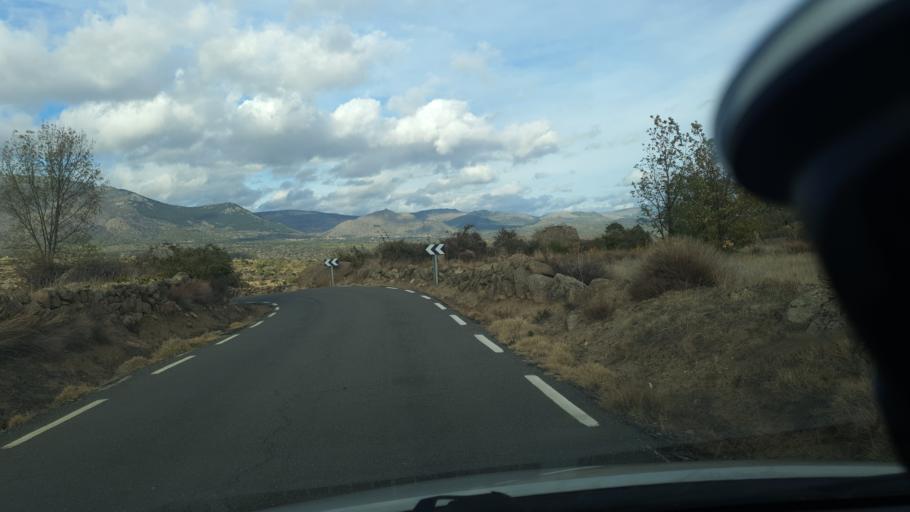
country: ES
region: Castille and Leon
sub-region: Provincia de Avila
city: Burgohondo
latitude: 40.4102
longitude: -4.8129
